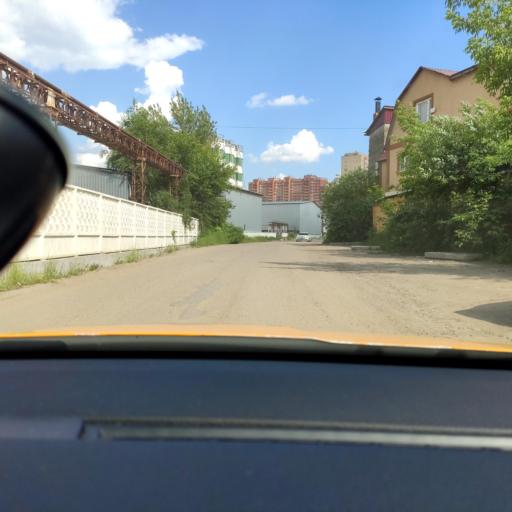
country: RU
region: Moskovskaya
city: Kotel'niki
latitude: 55.6441
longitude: 37.8507
